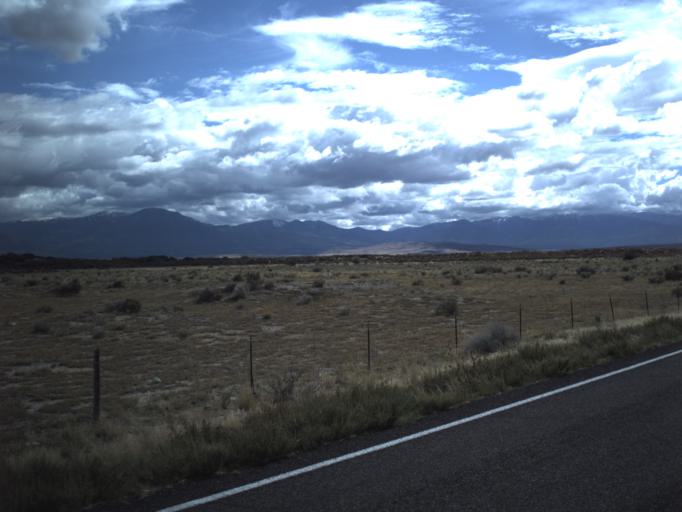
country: US
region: Utah
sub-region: Millard County
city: Fillmore
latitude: 39.1372
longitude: -112.4097
